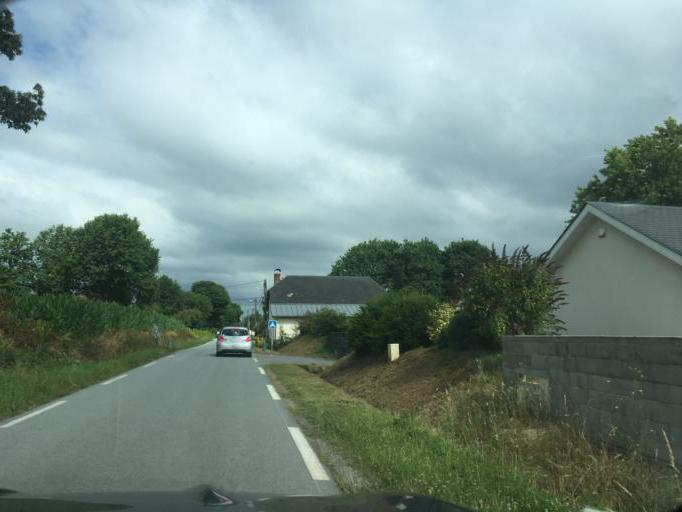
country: FR
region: Aquitaine
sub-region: Departement des Pyrenees-Atlantiques
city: Ousse
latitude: 43.3131
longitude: -0.2834
